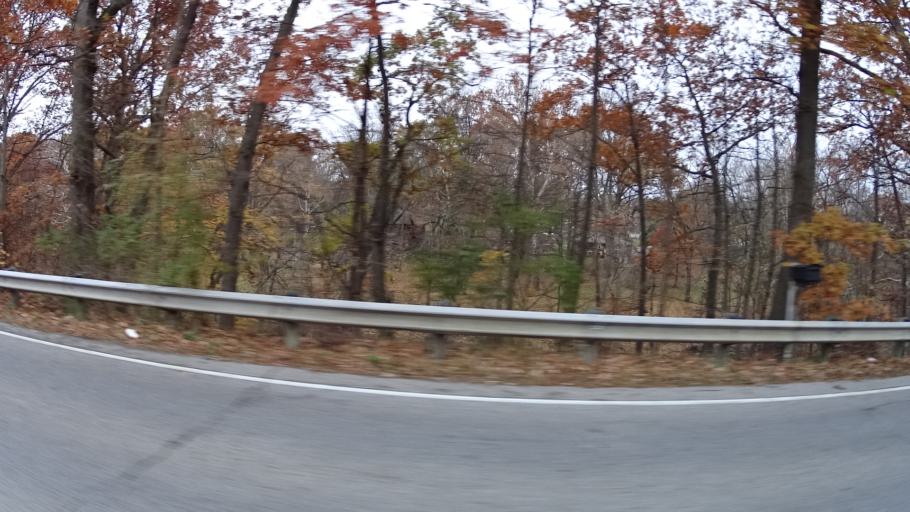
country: US
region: Ohio
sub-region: Lorain County
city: Elyria
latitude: 41.3432
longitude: -82.0905
